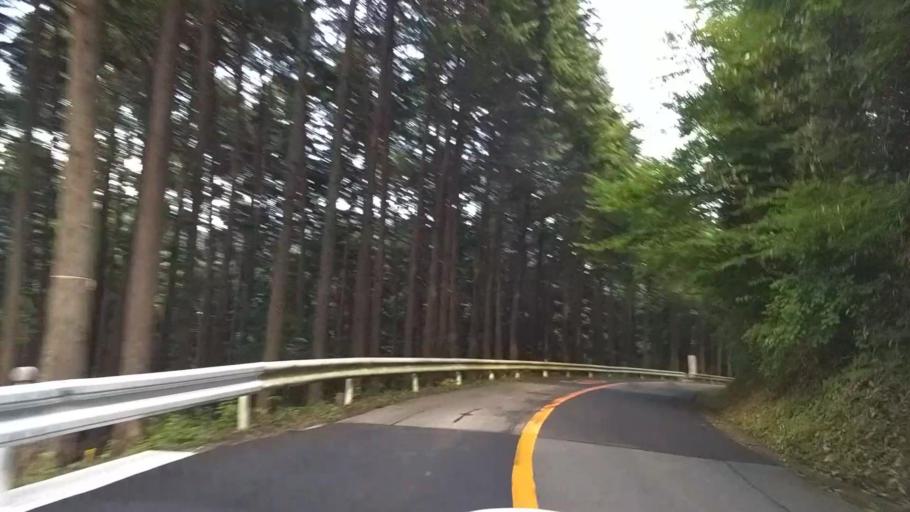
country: JP
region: Yamanashi
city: Uenohara
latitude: 35.6122
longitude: 139.2103
